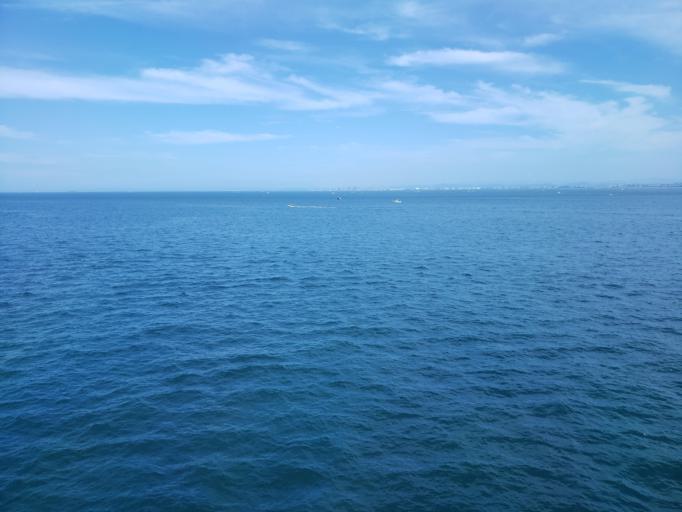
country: JP
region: Hyogo
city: Akashi
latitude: 34.6091
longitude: 134.9294
